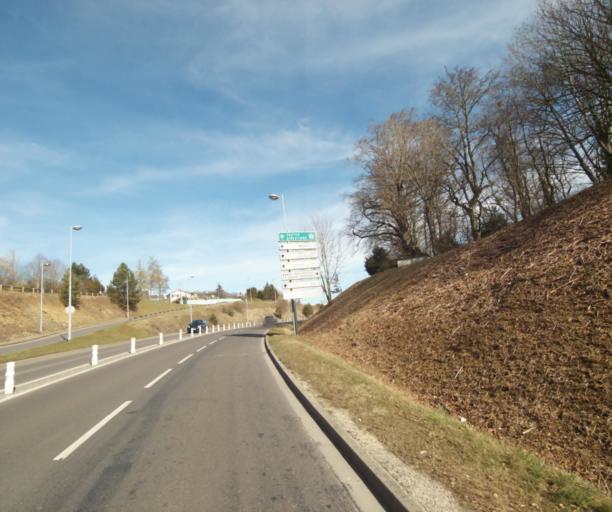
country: FR
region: Lorraine
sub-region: Departement de Meurthe-et-Moselle
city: Laxou
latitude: 48.6870
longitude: 6.1314
